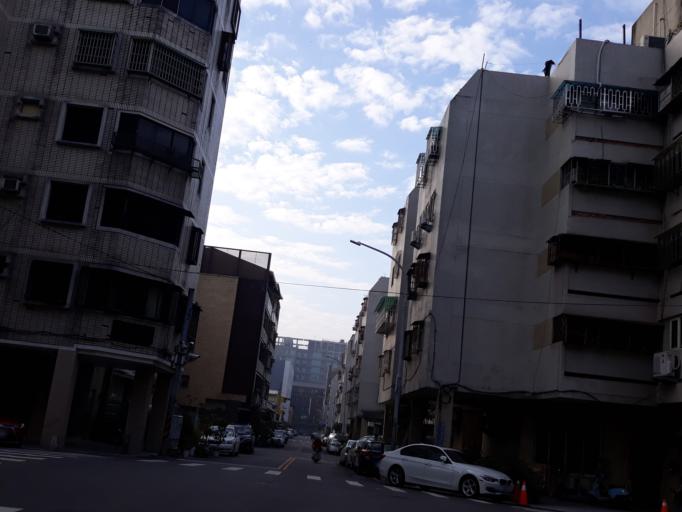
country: TW
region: Taiwan
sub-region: Taichung City
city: Taichung
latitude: 24.1492
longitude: 120.6676
